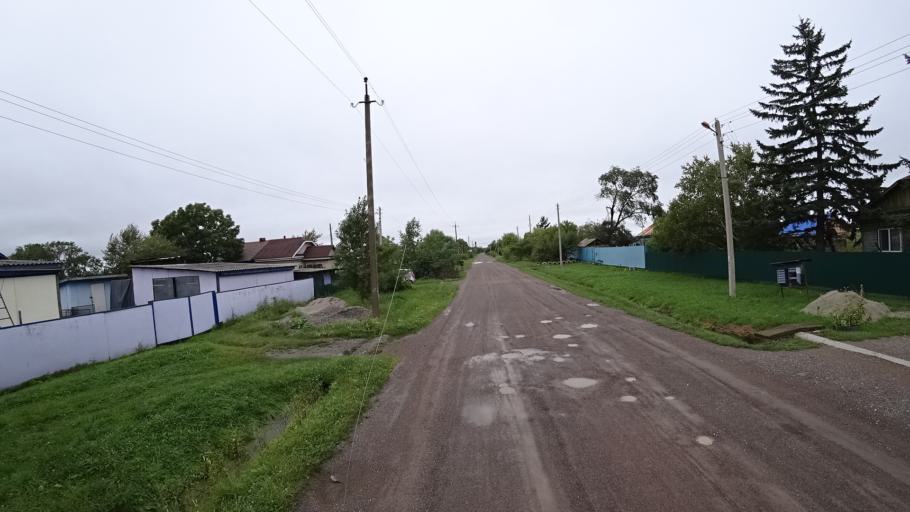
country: RU
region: Primorskiy
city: Monastyrishche
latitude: 44.1975
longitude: 132.4580
